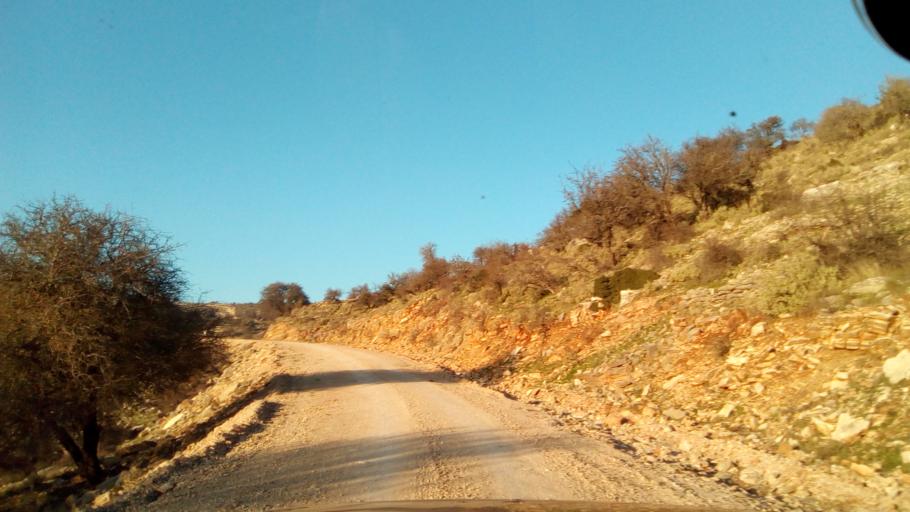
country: GR
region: West Greece
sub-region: Nomos Aitolias kai Akarnanias
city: Nafpaktos
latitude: 38.4524
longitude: 21.8437
